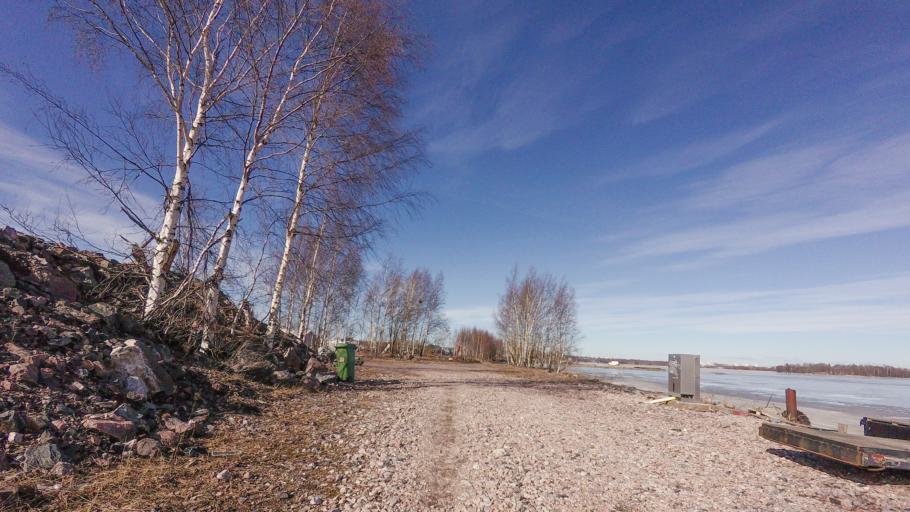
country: FI
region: Uusimaa
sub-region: Helsinki
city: Helsinki
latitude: 60.1938
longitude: 24.9850
